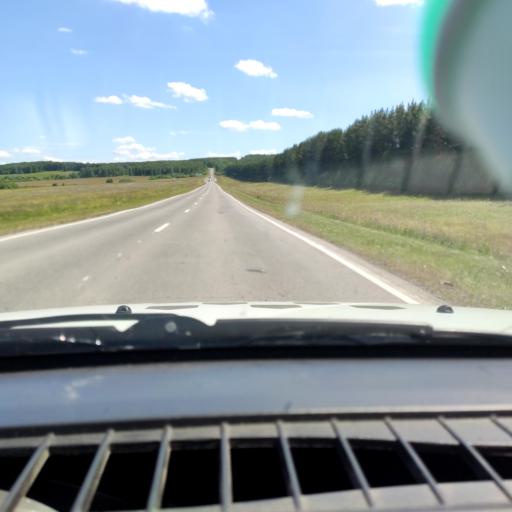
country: RU
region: Bashkortostan
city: Verkhniye Kigi
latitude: 55.3939
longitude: 58.6478
